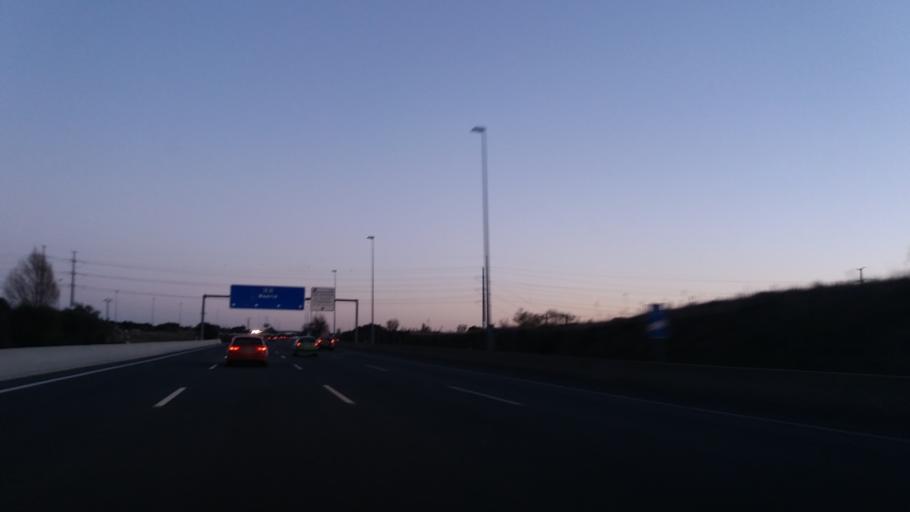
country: ES
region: Madrid
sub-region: Provincia de Madrid
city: Collado-Villalba
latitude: 40.6188
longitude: -3.9850
